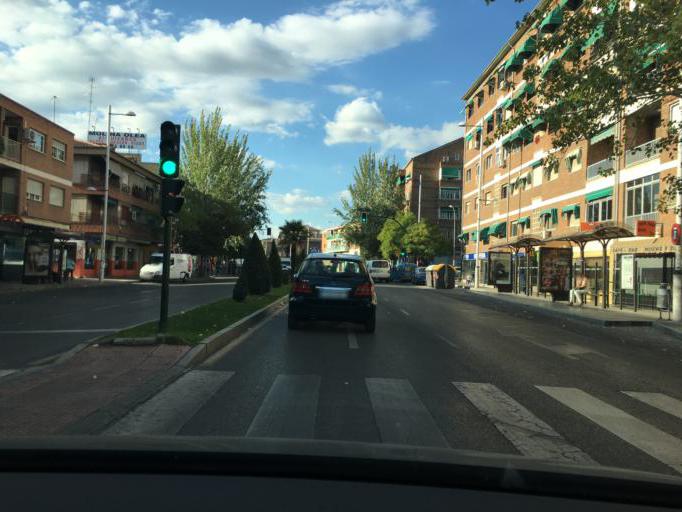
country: ES
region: Andalusia
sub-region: Provincia de Granada
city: Granada
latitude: 37.1937
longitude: -3.6084
